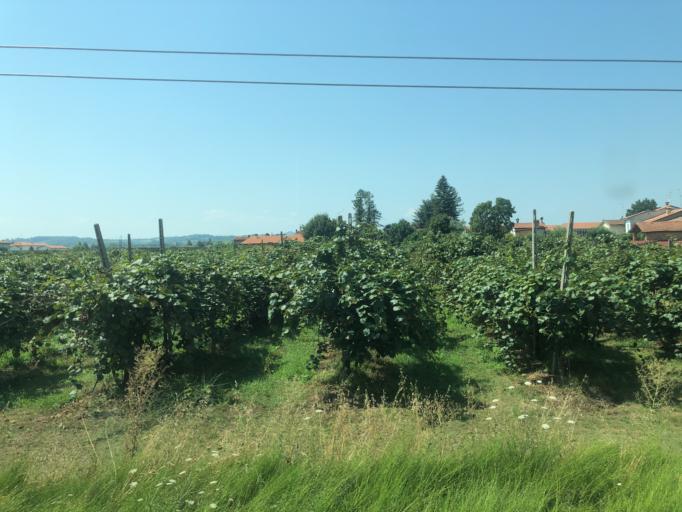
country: IT
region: Emilia-Romagna
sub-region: Provincia di Ravenna
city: Castel Bolognese
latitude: 44.3228
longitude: 11.8105
